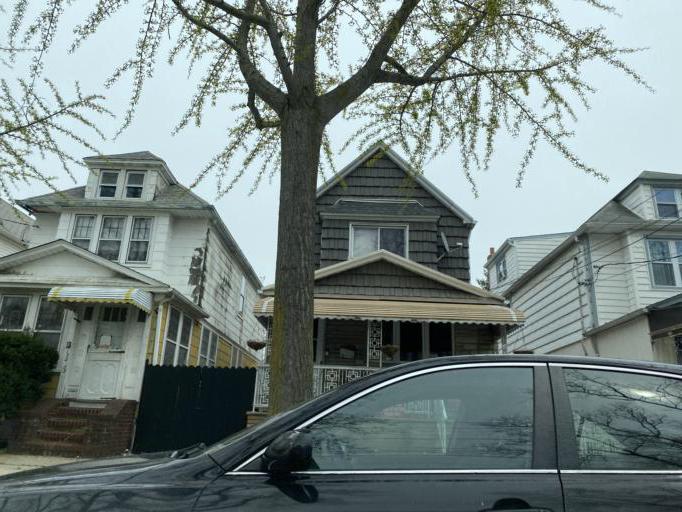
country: US
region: New York
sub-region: Queens County
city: Borough of Queens
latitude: 40.6735
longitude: -73.8257
